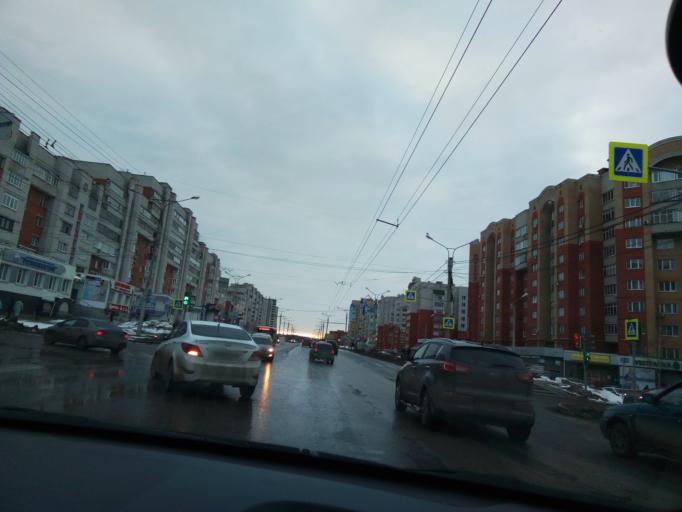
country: RU
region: Chuvashia
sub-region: Cheboksarskiy Rayon
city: Cheboksary
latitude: 56.1488
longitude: 47.1785
